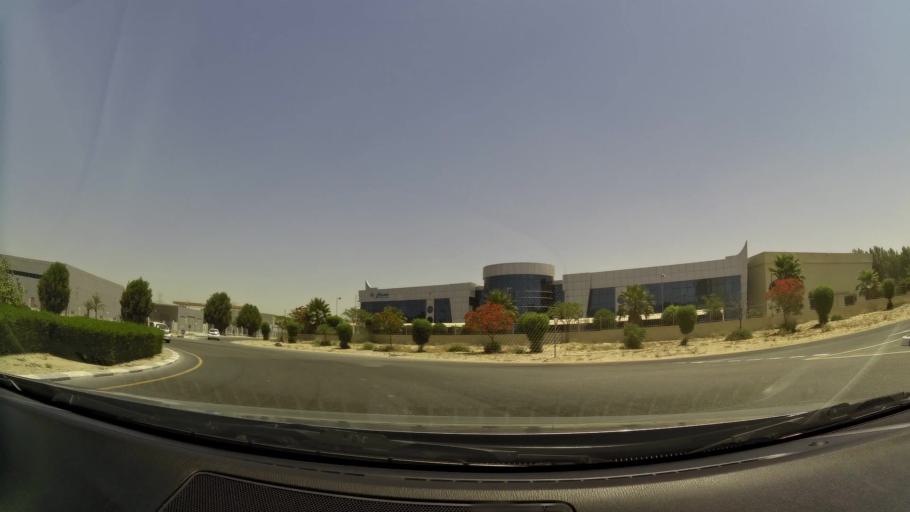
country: AE
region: Dubai
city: Dubai
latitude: 24.9851
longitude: 55.2073
